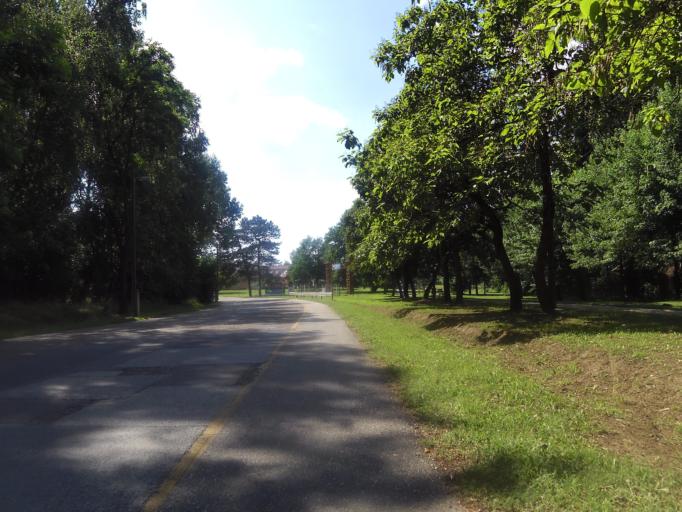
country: HU
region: Jasz-Nagykun-Szolnok
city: Tiszafured
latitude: 47.6221
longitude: 20.7393
